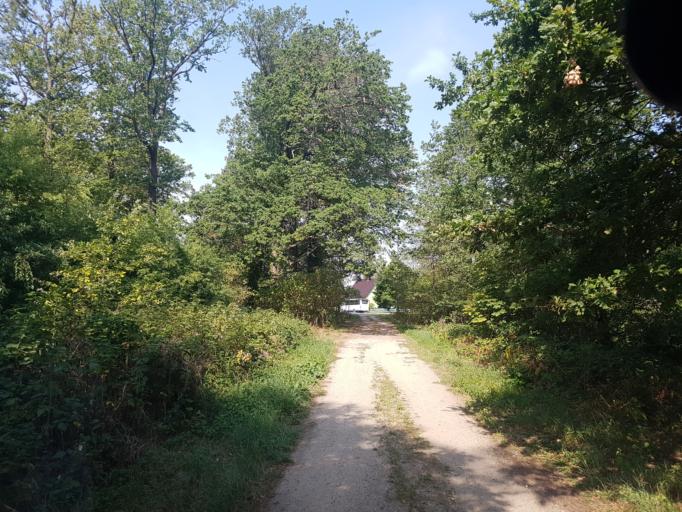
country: DE
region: Brandenburg
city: Sonnewalde
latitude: 51.6872
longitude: 13.6912
